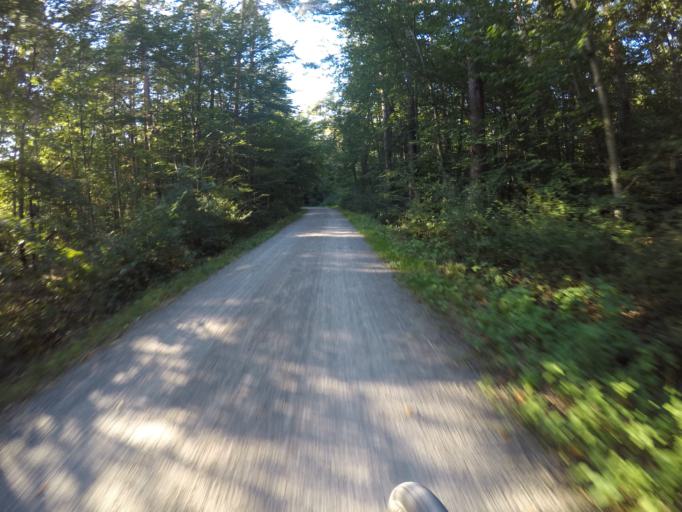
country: DE
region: Baden-Wuerttemberg
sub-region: Tuebingen Region
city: Dettenhausen
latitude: 48.6323
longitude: 9.0971
